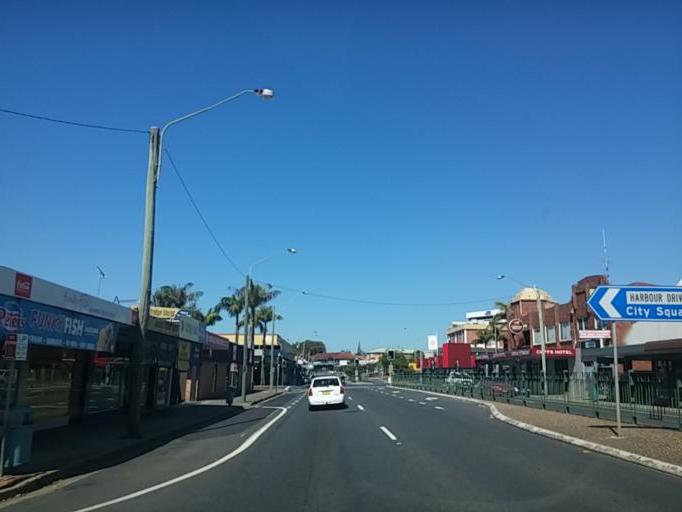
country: AU
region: New South Wales
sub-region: Coffs Harbour
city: Coffs Harbour
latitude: -30.2955
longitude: 153.1147
